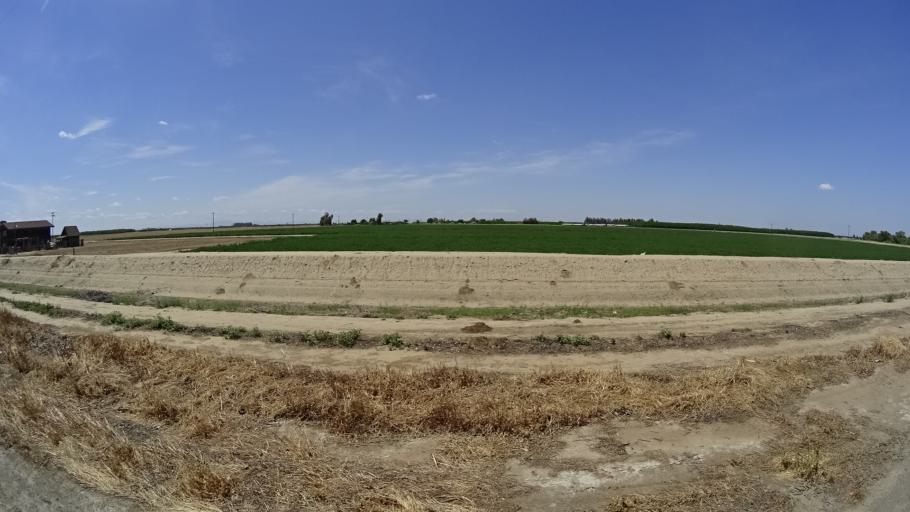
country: US
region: California
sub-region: Kings County
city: Home Garden
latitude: 36.2851
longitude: -119.6728
